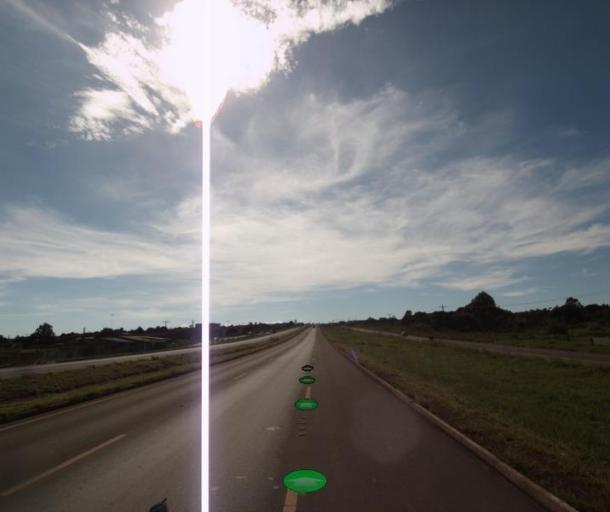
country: BR
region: Federal District
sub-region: Brasilia
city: Brasilia
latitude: -15.7402
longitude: -48.3082
